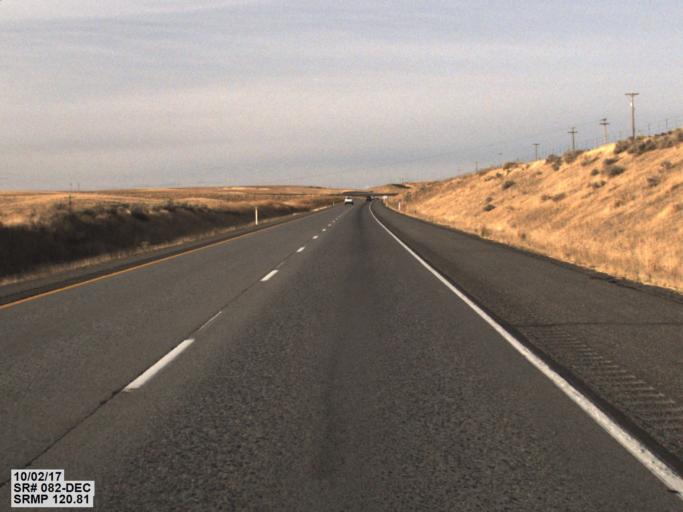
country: US
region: Washington
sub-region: Benton County
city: Highland
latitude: 46.0535
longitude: -119.2239
